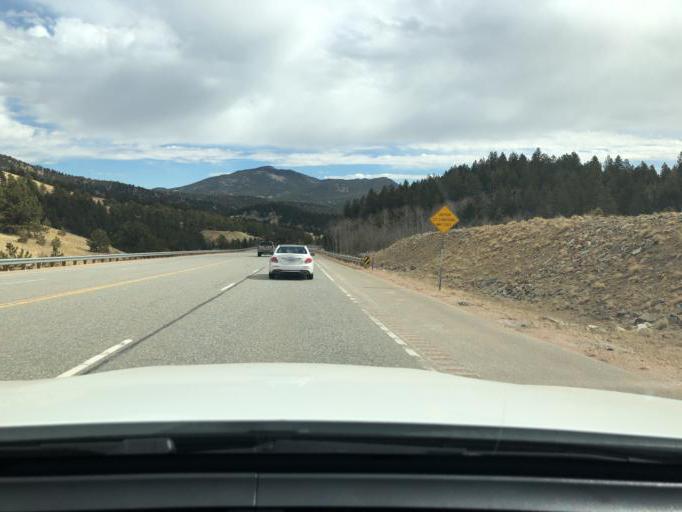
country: US
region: Colorado
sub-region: Gilpin County
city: Central City
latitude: 39.7856
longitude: -105.4909
